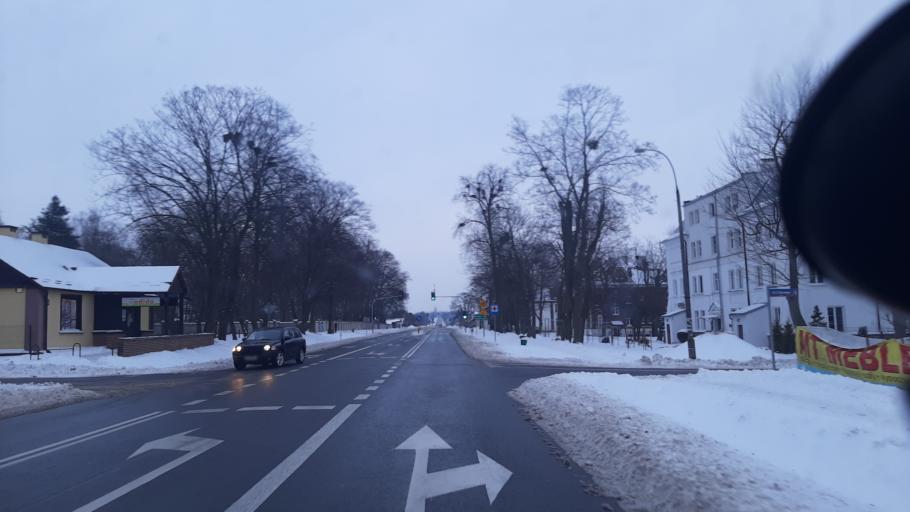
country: PL
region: Lublin Voivodeship
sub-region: Powiat lubelski
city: Garbow
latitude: 51.3649
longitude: 22.2958
